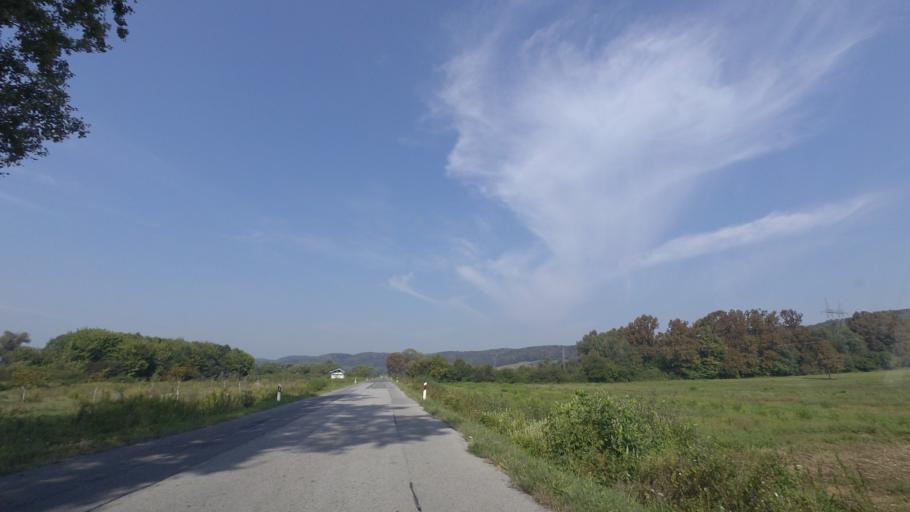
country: HR
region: Sisacko-Moslavacka
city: Hrvatska Kostajnica
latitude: 45.2276
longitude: 16.6136
